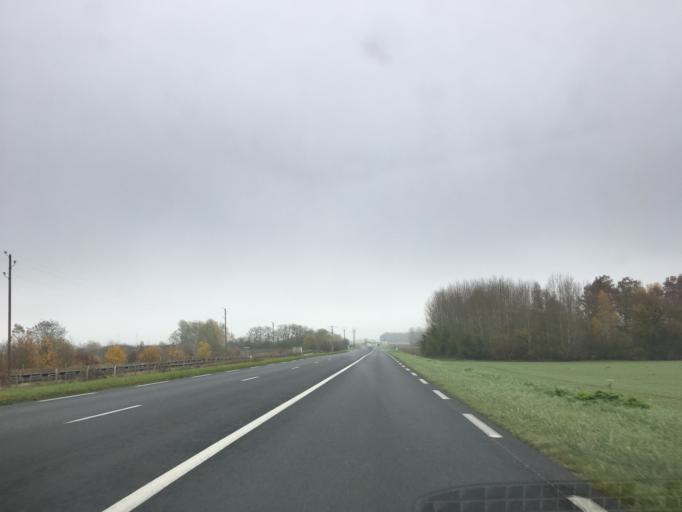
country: FR
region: Ile-de-France
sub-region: Departement de Seine-et-Marne
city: Varennes-sur-Seine
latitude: 48.3610
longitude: 2.9189
